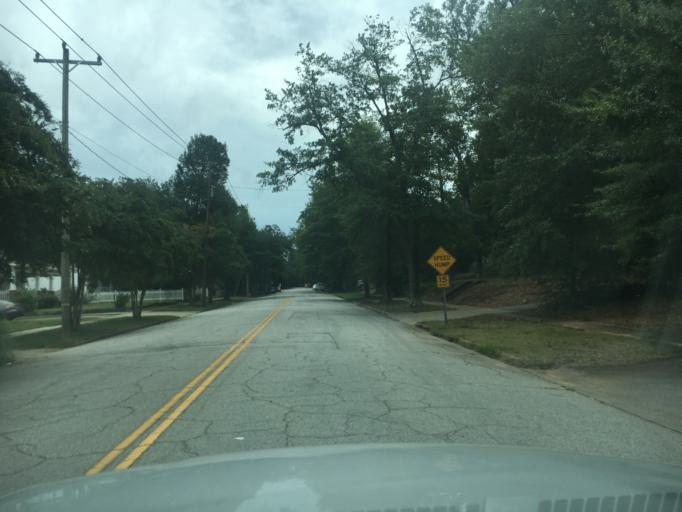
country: US
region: South Carolina
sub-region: Greenville County
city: Greenville
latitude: 34.8582
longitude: -82.4091
